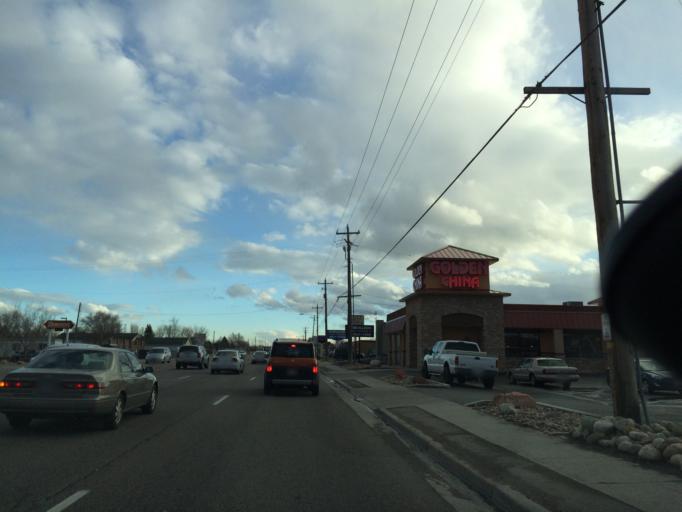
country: US
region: Utah
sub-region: Salt Lake County
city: Taylorsville
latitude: 40.6628
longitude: -111.9390
